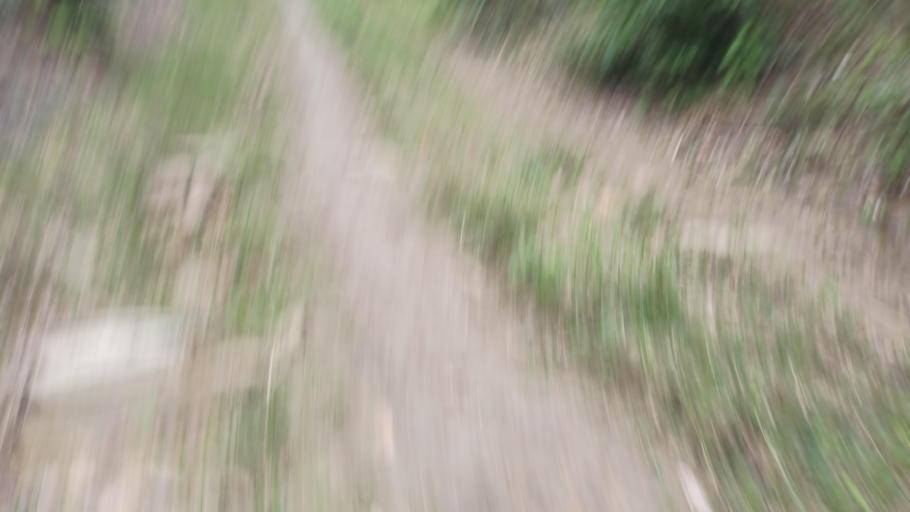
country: MX
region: Veracruz
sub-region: Coatzintla
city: Manuel Maria Contreras
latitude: 20.3511
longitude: -97.4655
